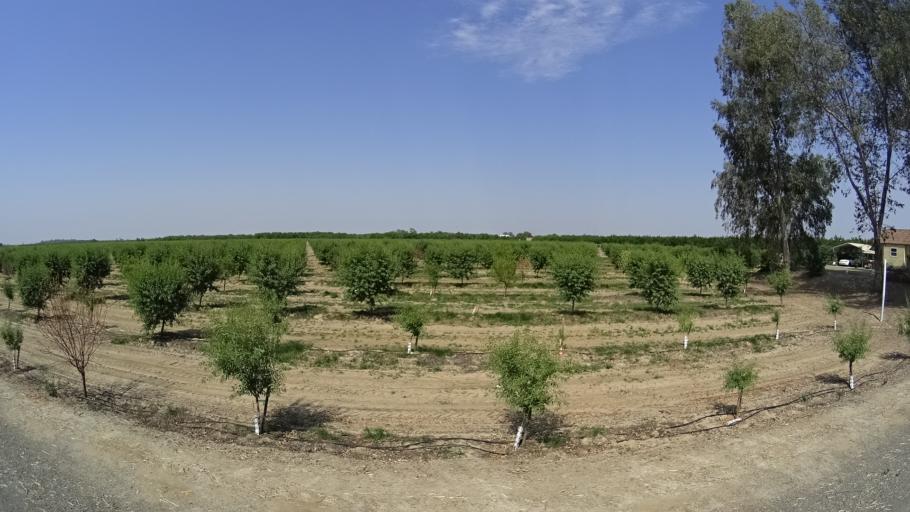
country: US
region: California
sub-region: Fresno County
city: Riverdale
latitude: 36.3998
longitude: -119.7983
